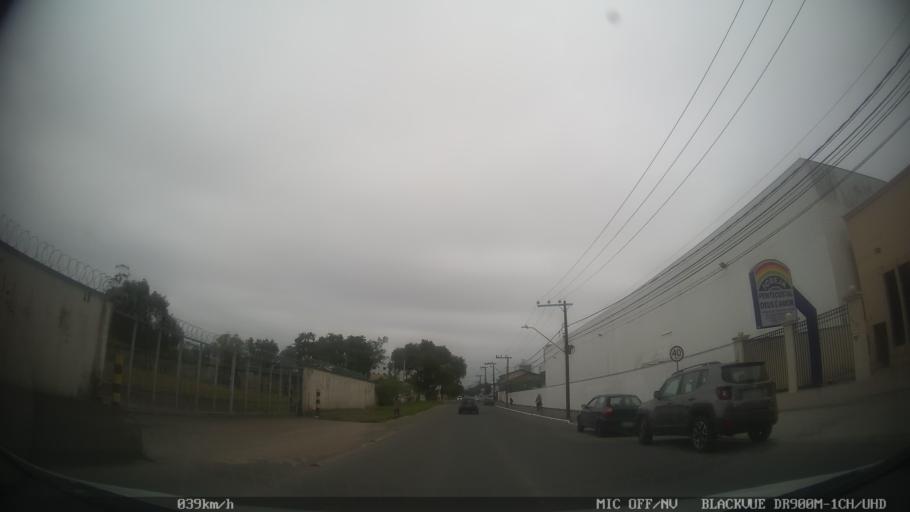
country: BR
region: Santa Catarina
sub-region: Joinville
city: Joinville
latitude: -26.3082
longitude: -48.8397
